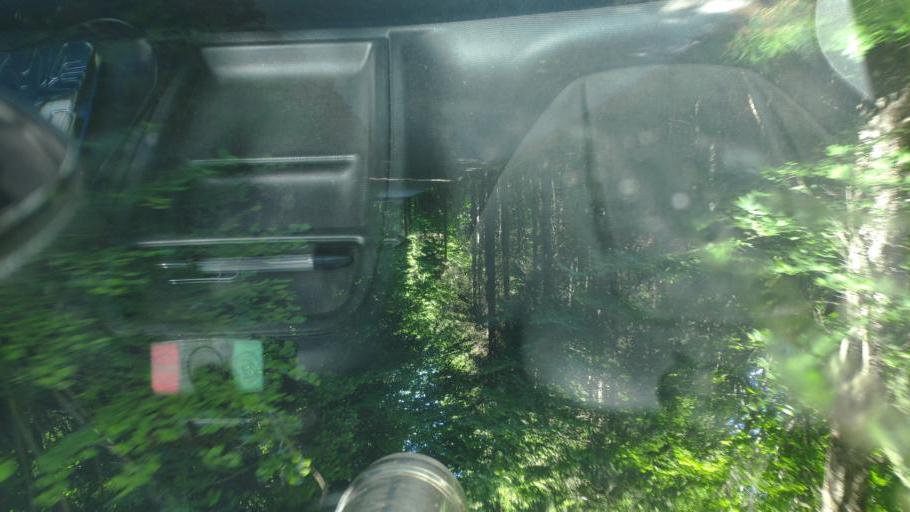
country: IT
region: Veneto
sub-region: Provincia di Vicenza
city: Cogollo del Cengio
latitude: 45.8218
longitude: 11.4405
